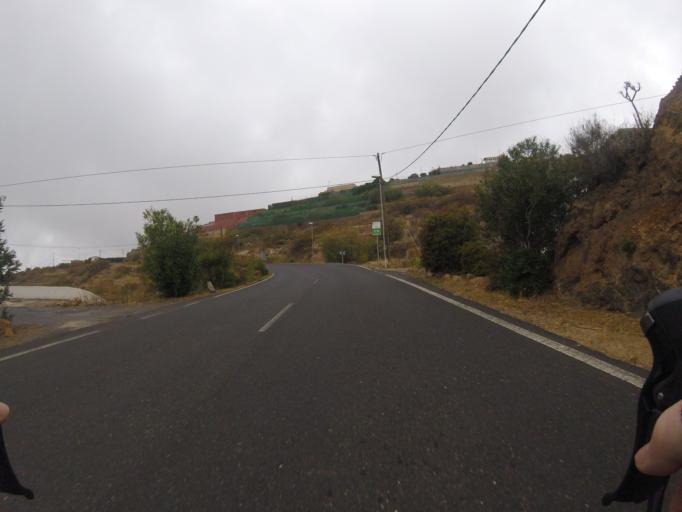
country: ES
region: Canary Islands
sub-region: Provincia de Santa Cruz de Tenerife
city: Guimar
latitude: 28.2885
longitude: -16.4057
